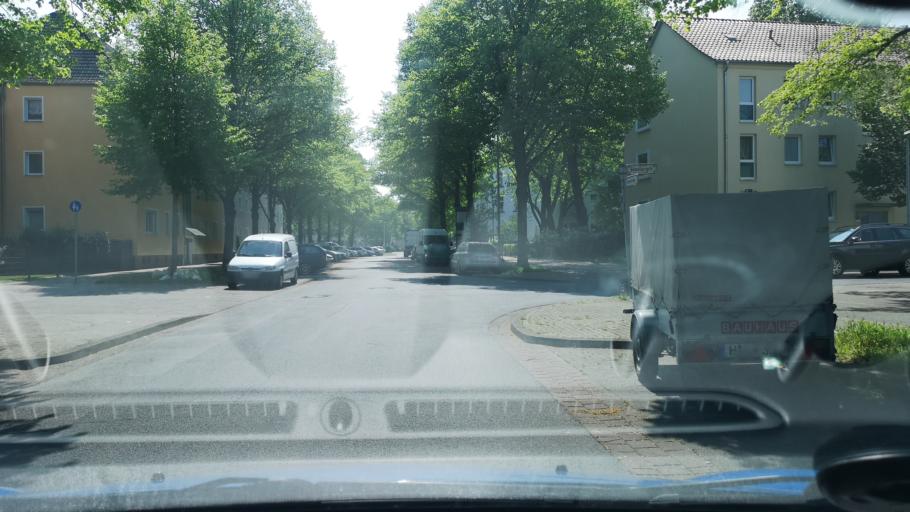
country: DE
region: Lower Saxony
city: Hannover
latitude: 52.3990
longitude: 9.7215
